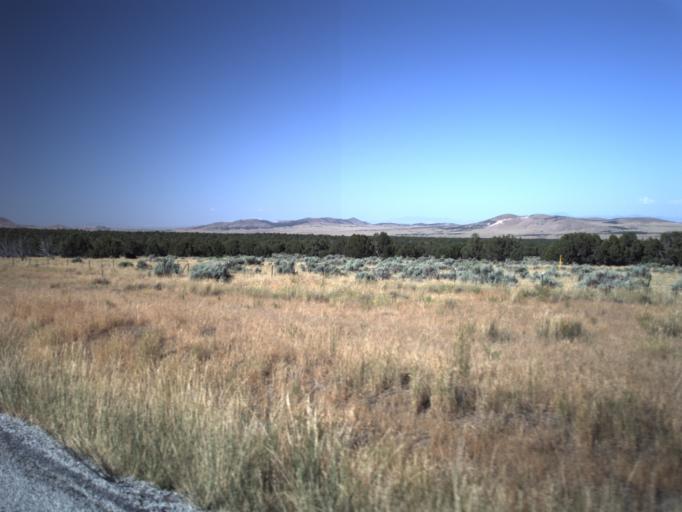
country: US
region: Utah
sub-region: Juab County
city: Mona
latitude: 39.7908
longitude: -112.1487
